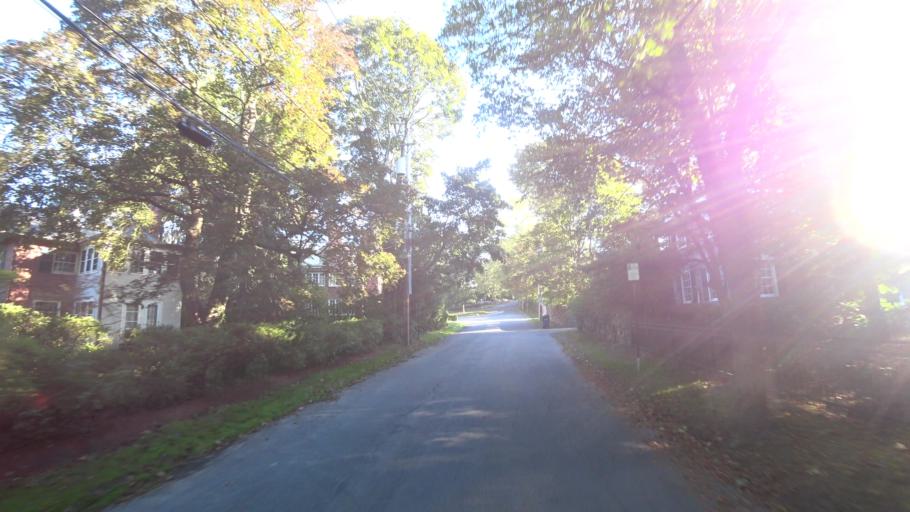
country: US
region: Massachusetts
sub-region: Middlesex County
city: Newton
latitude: 42.3300
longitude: -71.1727
